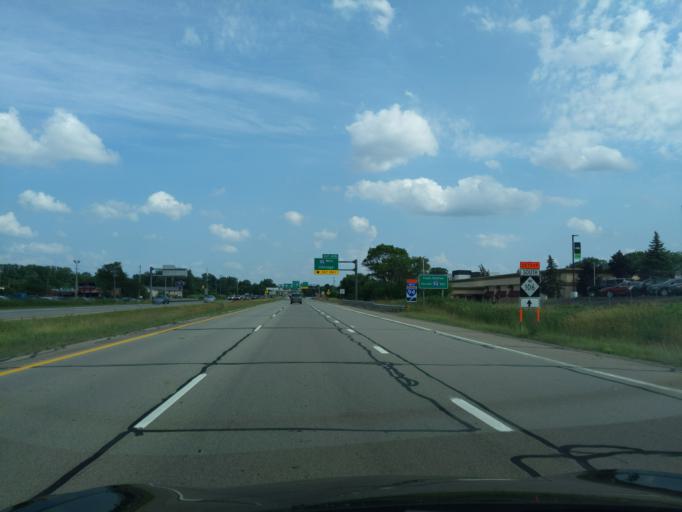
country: US
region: Michigan
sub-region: Jackson County
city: Jackson
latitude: 42.2775
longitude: -84.4312
